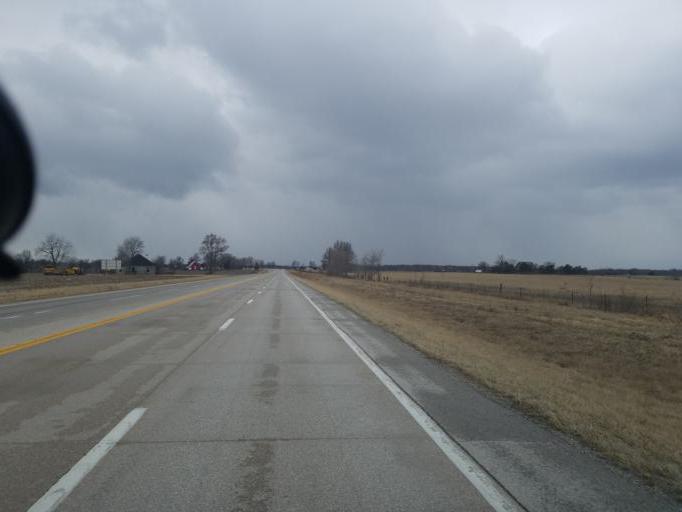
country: US
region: Missouri
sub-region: Macon County
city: Macon
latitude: 39.7943
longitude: -92.4779
